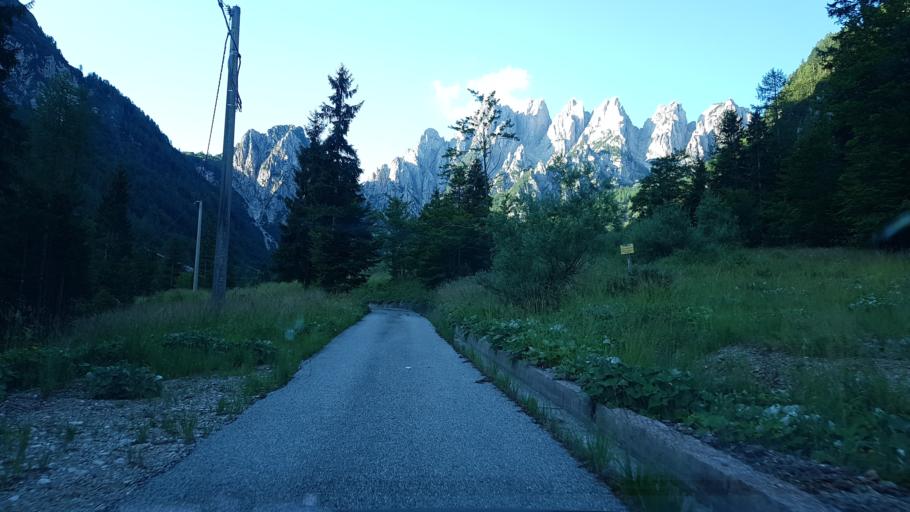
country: IT
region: Friuli Venezia Giulia
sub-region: Provincia di Udine
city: Pontebba
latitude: 46.4933
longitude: 13.2541
